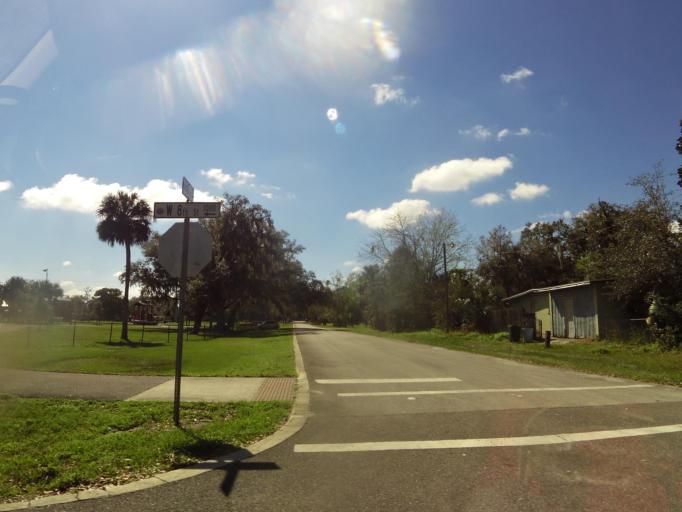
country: US
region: Florida
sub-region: Seminole County
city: Sanford
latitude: 28.8053
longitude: -81.2779
